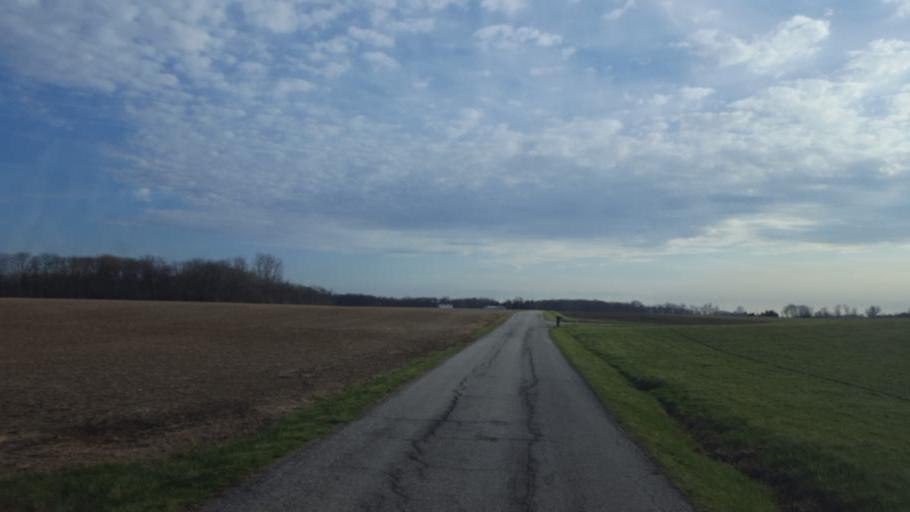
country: US
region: Ohio
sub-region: Crawford County
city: Bucyrus
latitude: 40.7246
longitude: -82.9365
